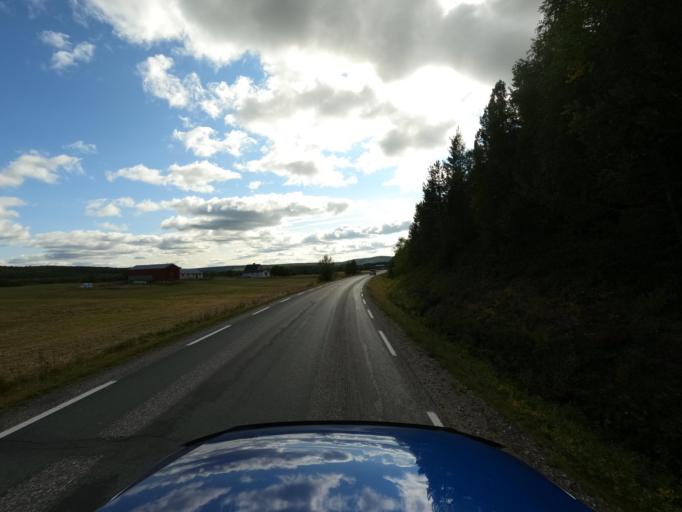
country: NO
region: Finnmark Fylke
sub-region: Karasjok
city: Karasjohka
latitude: 69.4119
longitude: 25.8040
